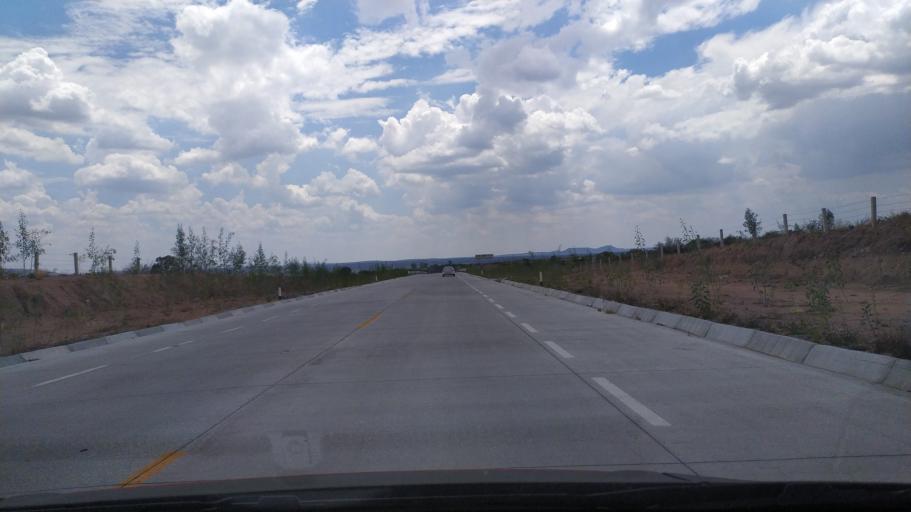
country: MX
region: Guanajuato
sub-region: San Francisco del Rincon
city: Estacion de San Francisco
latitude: 21.0870
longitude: -101.8120
